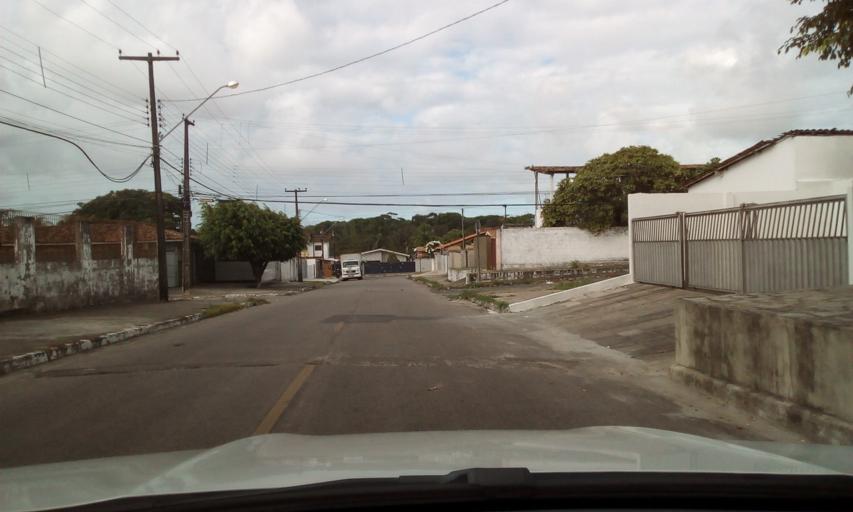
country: BR
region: Paraiba
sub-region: Joao Pessoa
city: Joao Pessoa
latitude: -7.1486
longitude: -34.8808
